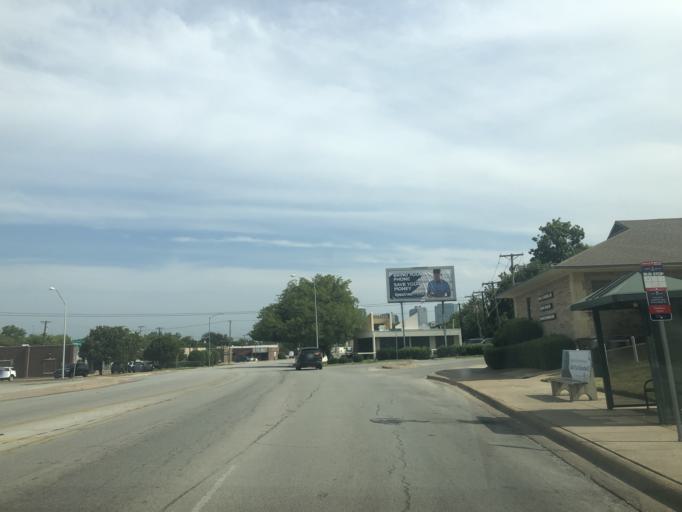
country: US
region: Texas
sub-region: Tarrant County
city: Fort Worth
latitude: 32.7349
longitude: -97.3316
